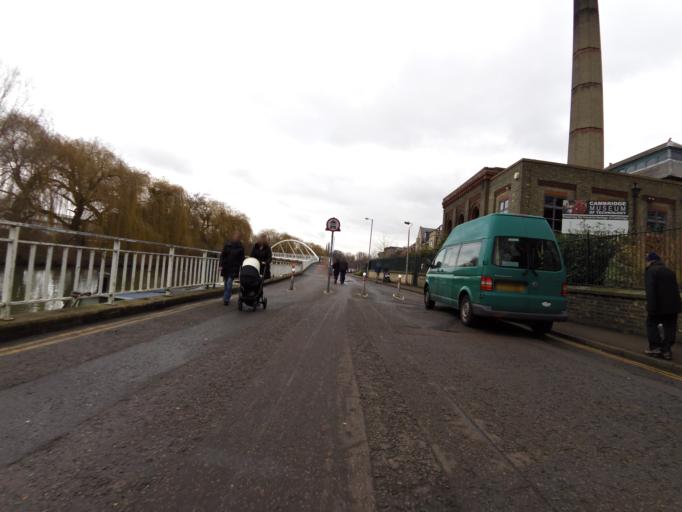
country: GB
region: England
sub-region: Cambridgeshire
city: Cambridge
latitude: 52.2126
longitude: 0.1426
